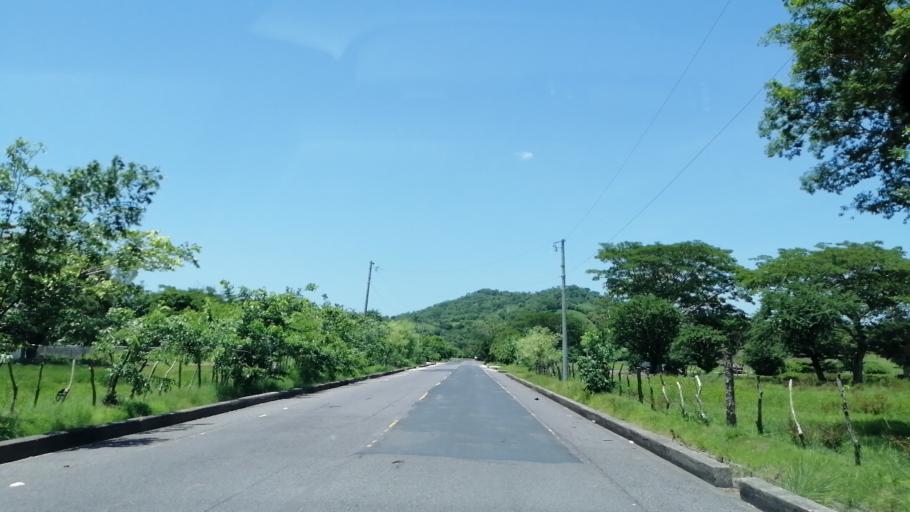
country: SV
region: Chalatenango
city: Chalatenango
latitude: 14.0332
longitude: -88.9609
